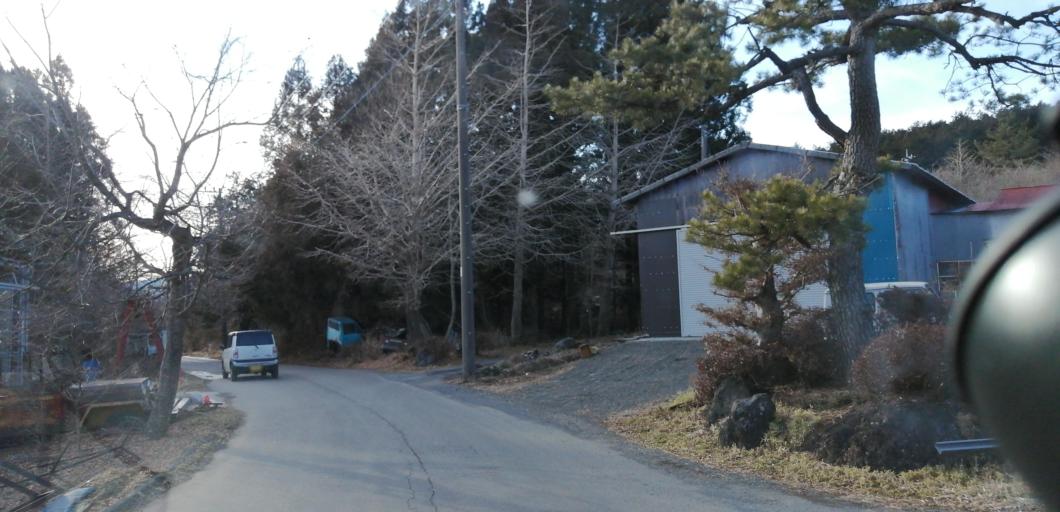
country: JP
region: Yamanashi
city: Fujikawaguchiko
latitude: 35.4022
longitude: 138.6074
